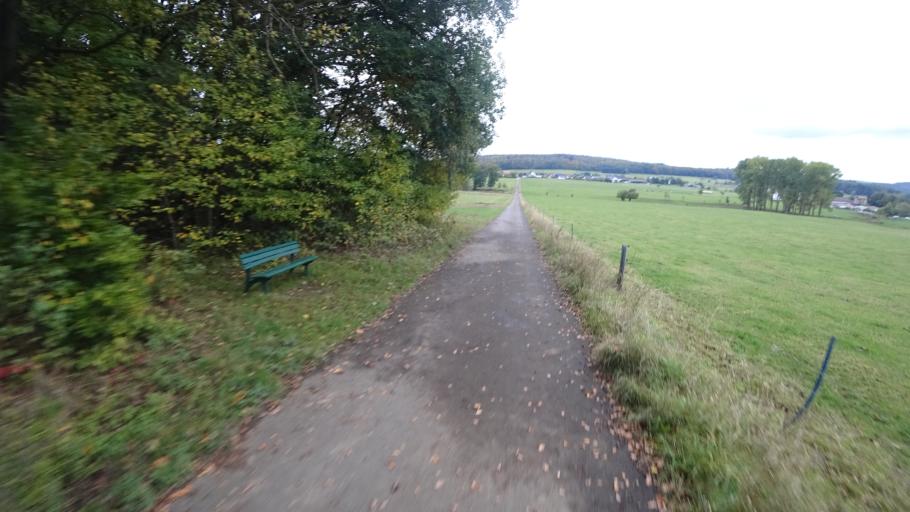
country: DE
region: Rheinland-Pfalz
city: Maxsain
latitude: 50.5516
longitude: 7.7795
